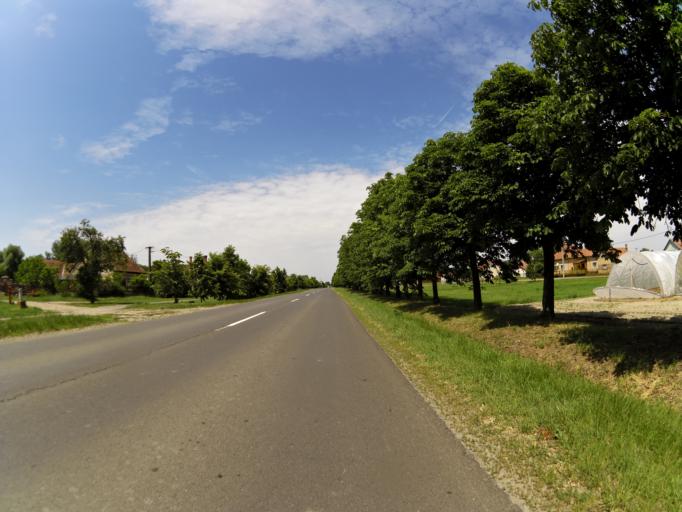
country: HU
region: Csongrad
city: Opusztaszer
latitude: 46.4924
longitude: 20.0685
